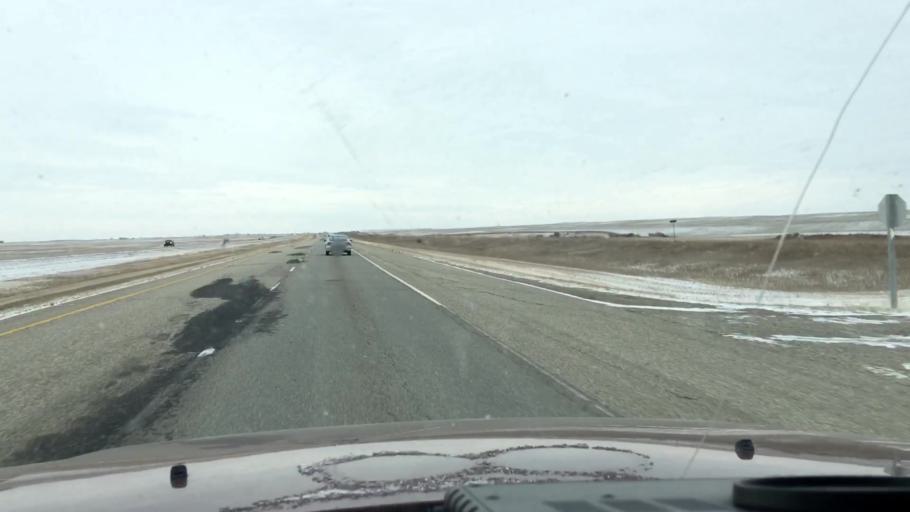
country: CA
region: Saskatchewan
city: Saskatoon
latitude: 51.4637
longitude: -106.2382
